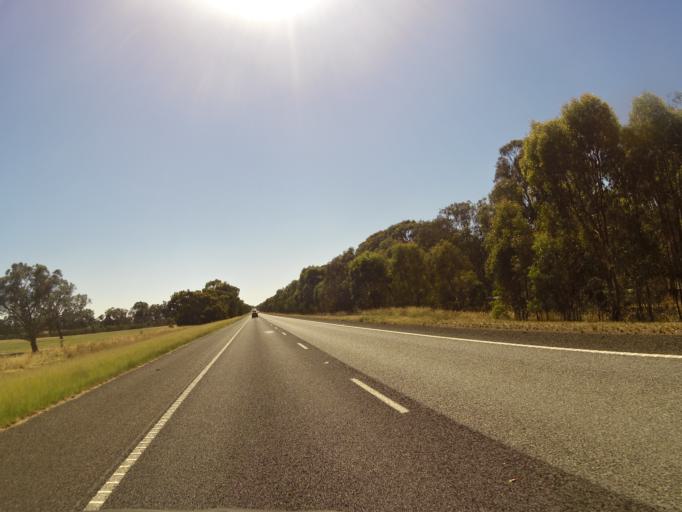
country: AU
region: Victoria
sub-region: Greater Shepparton
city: Shepparton
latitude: -36.8448
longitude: 145.3513
